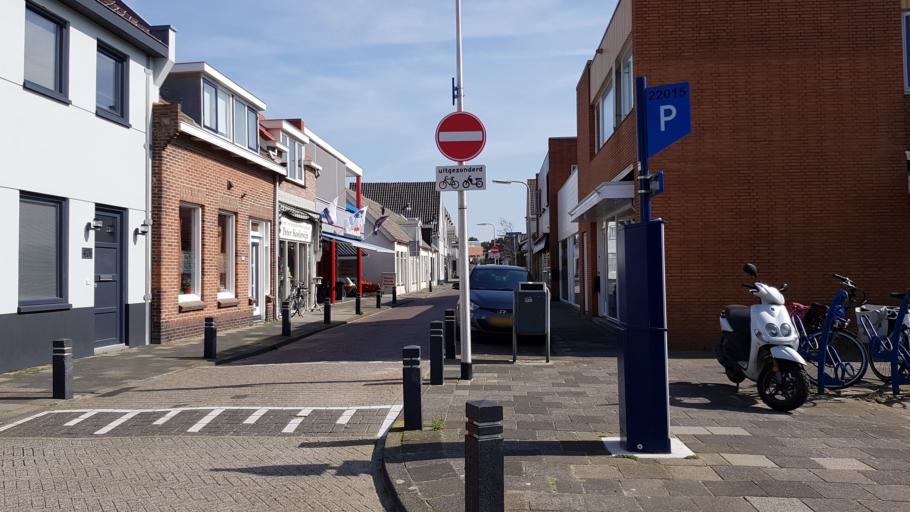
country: NL
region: South Holland
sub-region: Gemeente Noordwijk
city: Noordwijk-Binnen
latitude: 52.2450
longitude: 4.4332
